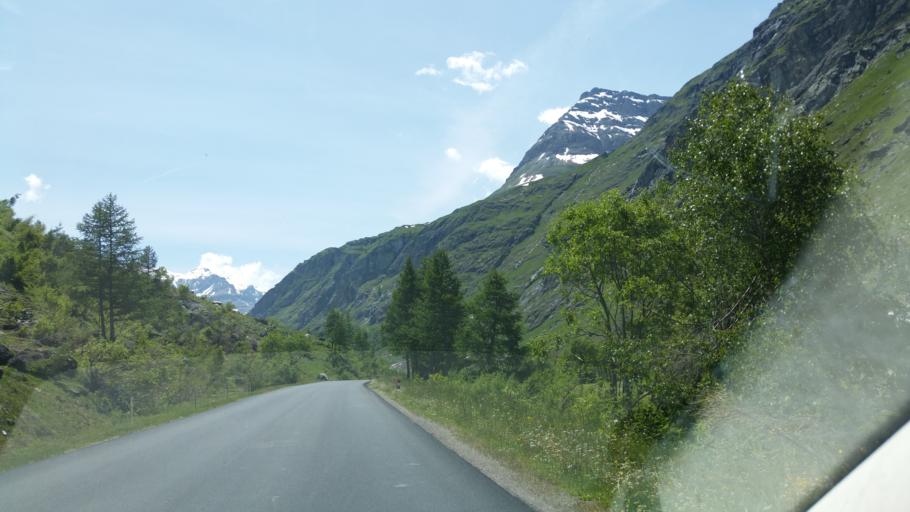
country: FR
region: Rhone-Alpes
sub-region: Departement de la Savoie
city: Val-d'Isere
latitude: 45.3644
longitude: 7.0371
